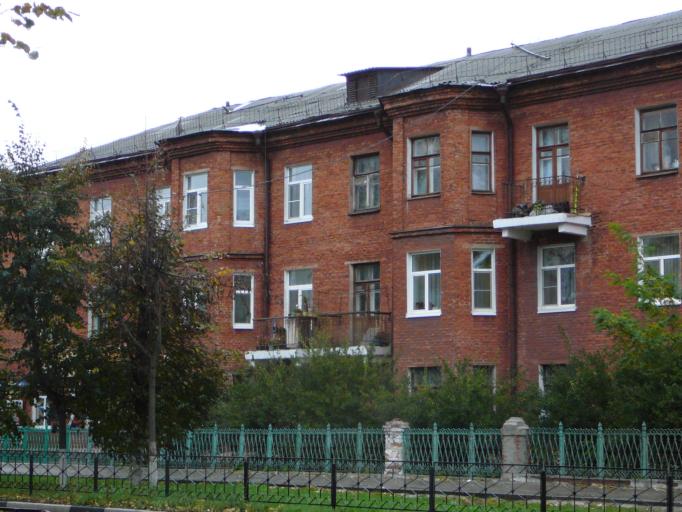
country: RU
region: Moskovskaya
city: Shatura
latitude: 55.5754
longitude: 39.5381
